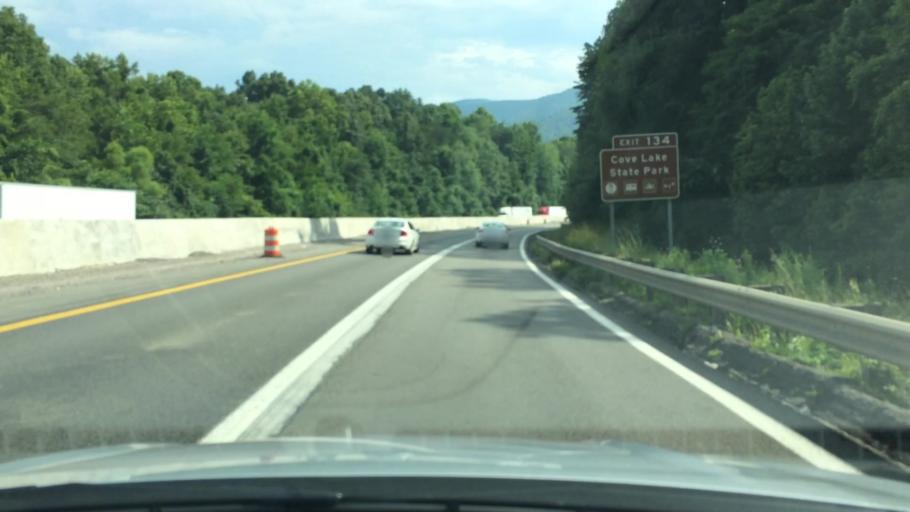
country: US
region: Tennessee
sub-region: Campbell County
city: Caryville
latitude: 36.3213
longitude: -84.2259
